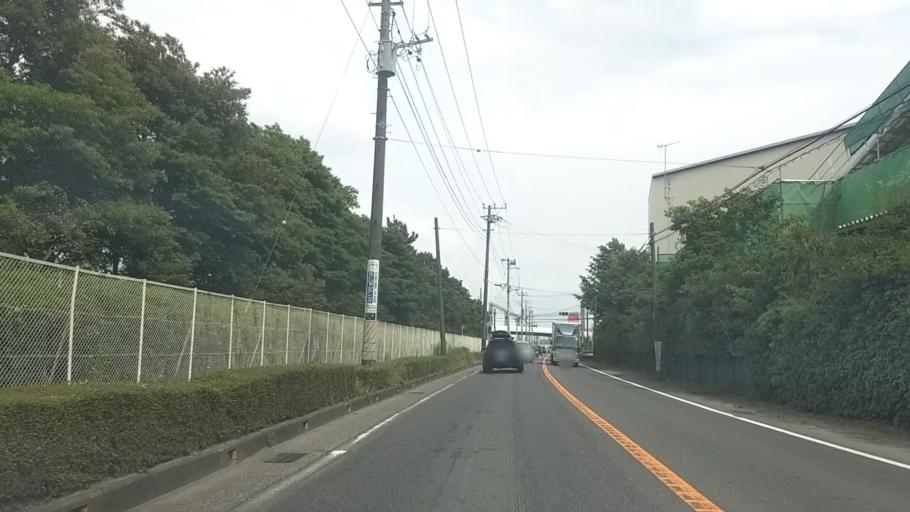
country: JP
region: Kanagawa
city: Fujisawa
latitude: 35.3954
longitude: 139.4529
